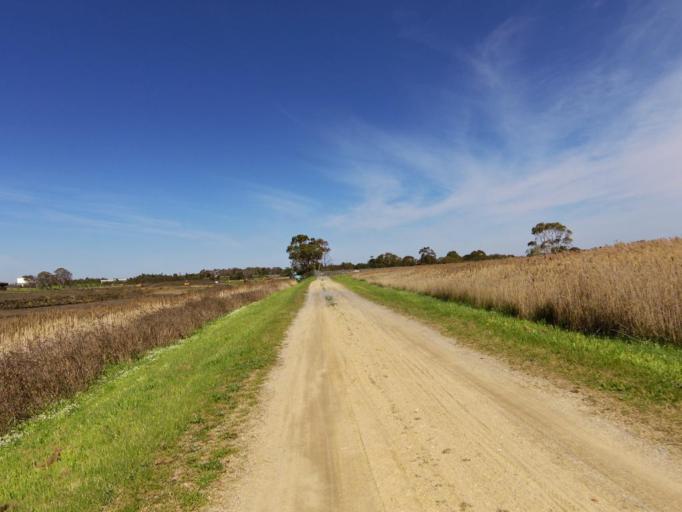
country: AU
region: Victoria
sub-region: Greater Dandenong
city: Keysborough
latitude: -38.0288
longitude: 145.1864
